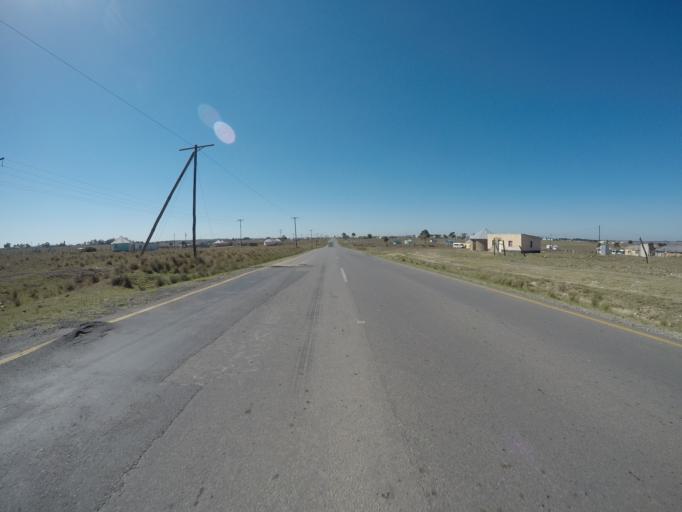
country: ZA
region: Eastern Cape
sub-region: OR Tambo District Municipality
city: Mthatha
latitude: -31.8983
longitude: 28.7882
